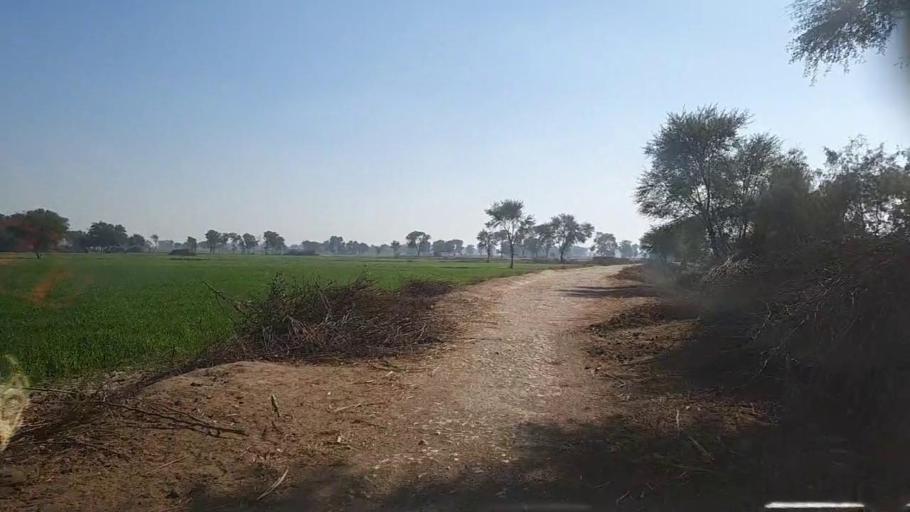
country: PK
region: Sindh
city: Khairpur
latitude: 28.0474
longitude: 69.8189
